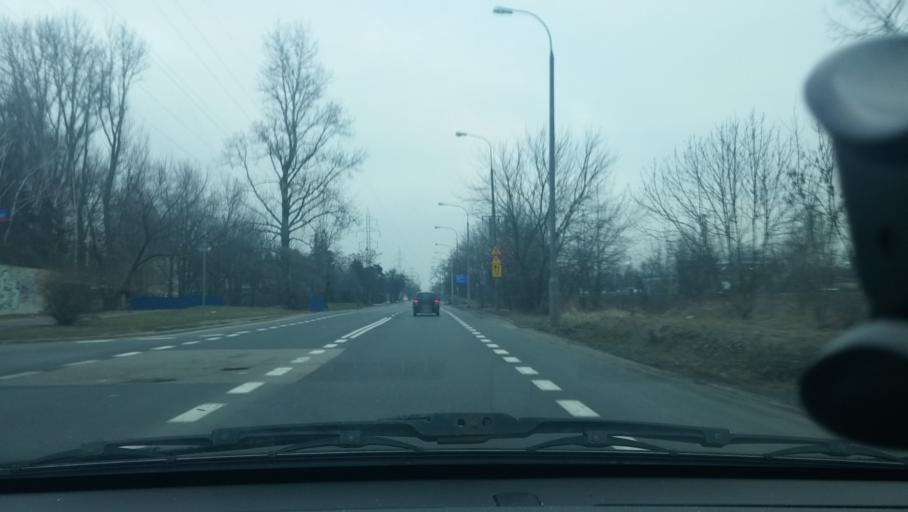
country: PL
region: Masovian Voivodeship
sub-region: Warszawa
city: Wawer
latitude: 52.2160
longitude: 21.1574
